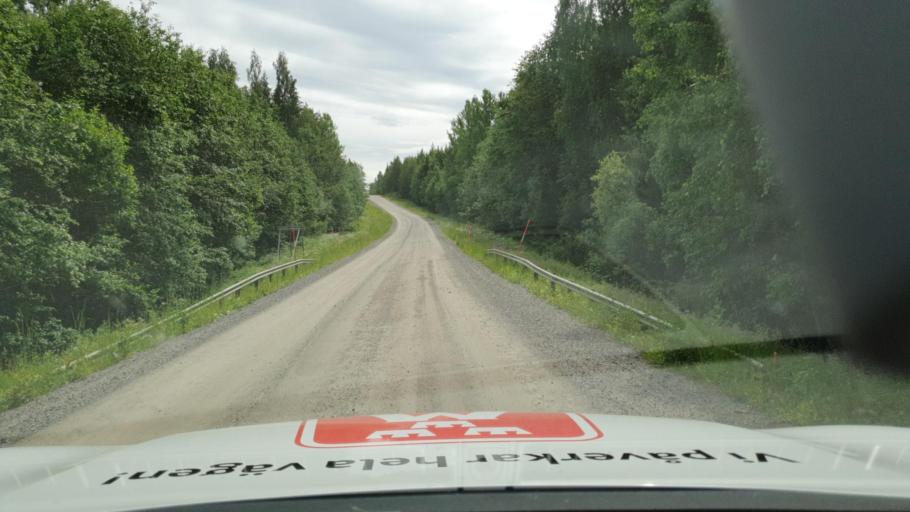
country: SE
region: Vaesterbotten
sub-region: Skelleftea Kommun
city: Burtraesk
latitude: 64.3964
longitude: 20.4086
